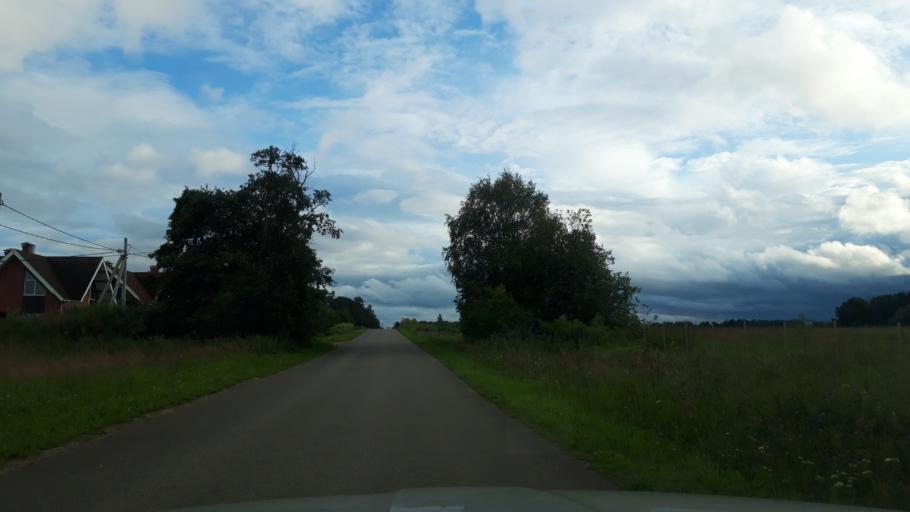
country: RU
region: Moskovskaya
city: Istra
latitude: 56.0979
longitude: 36.7992
